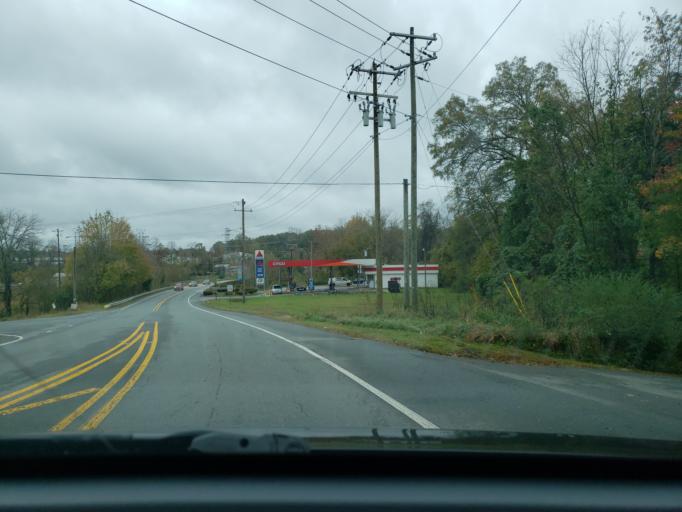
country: US
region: North Carolina
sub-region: Stokes County
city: Walnut Cove
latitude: 36.2932
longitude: -80.1418
